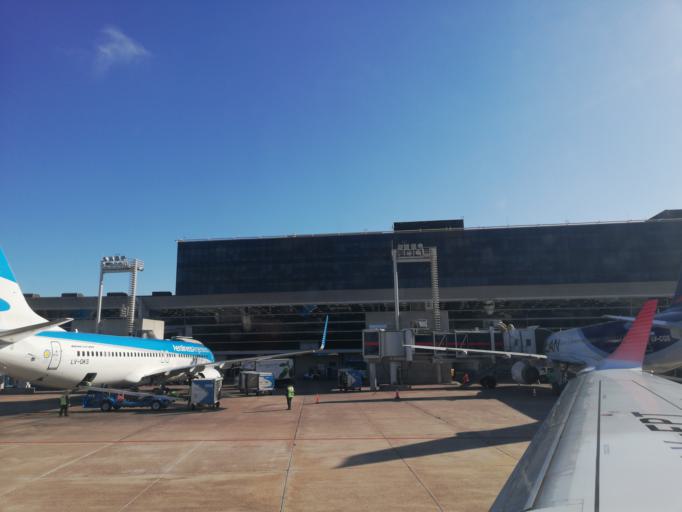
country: AR
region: Buenos Aires F.D.
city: Retiro
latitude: -34.5583
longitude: -58.4128
